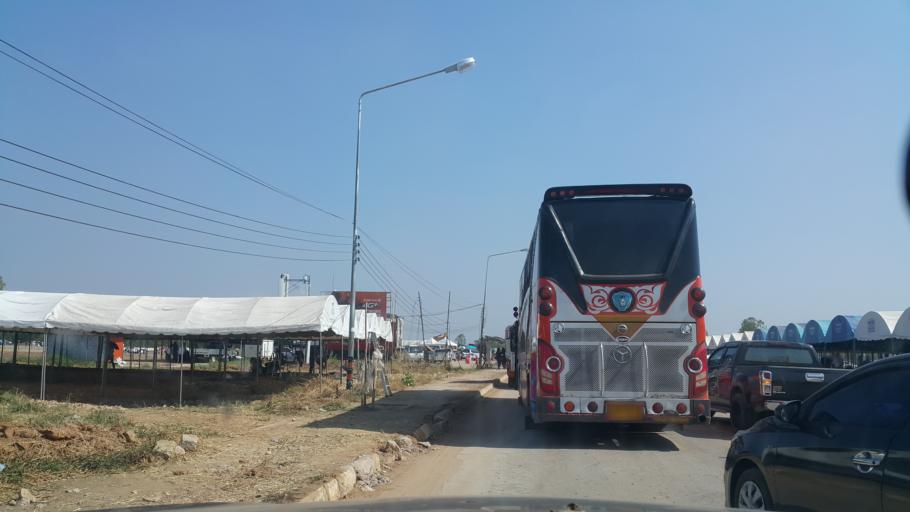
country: TH
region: Khon Kaen
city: Khon Kaen
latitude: 16.5128
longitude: 102.8708
